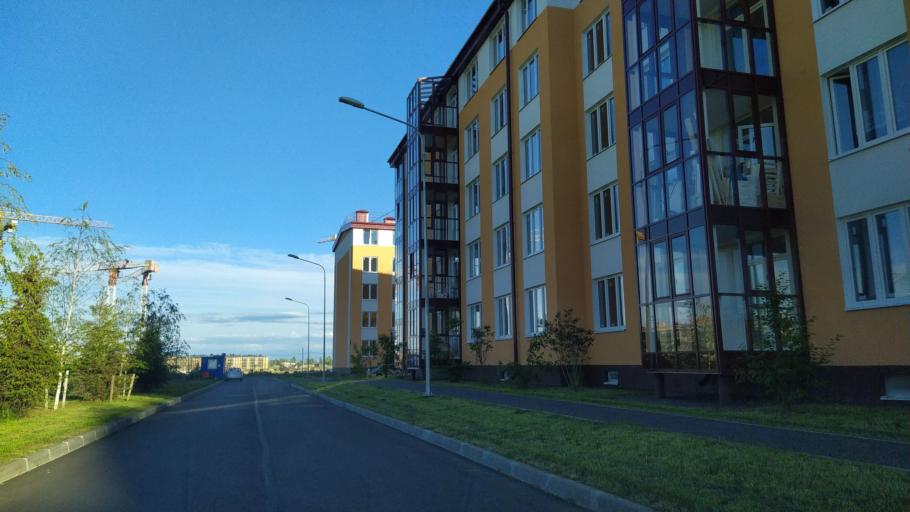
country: RU
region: St.-Petersburg
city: Aleksandrovskaya
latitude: 59.7541
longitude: 30.3607
